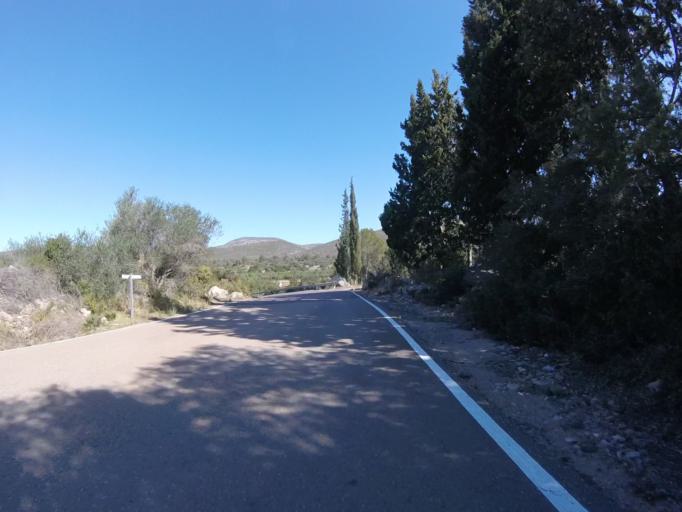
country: ES
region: Valencia
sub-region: Provincia de Castello
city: Santa Magdalena de Pulpis
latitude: 40.3703
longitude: 0.2744
